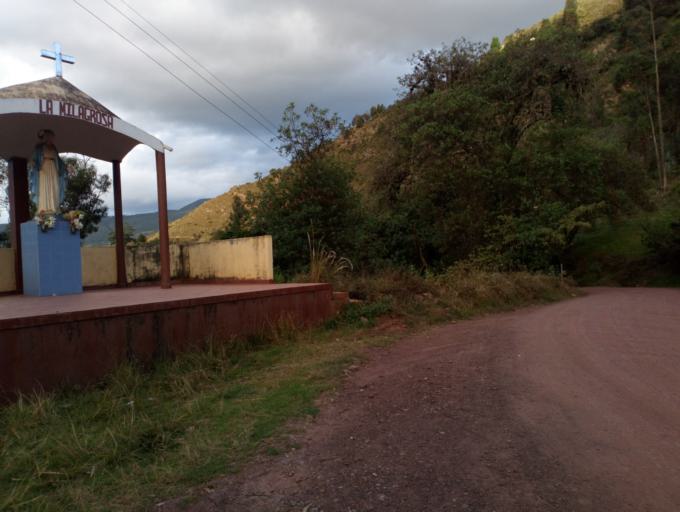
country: CO
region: Boyaca
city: Susacon
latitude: 6.1288
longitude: -72.7092
